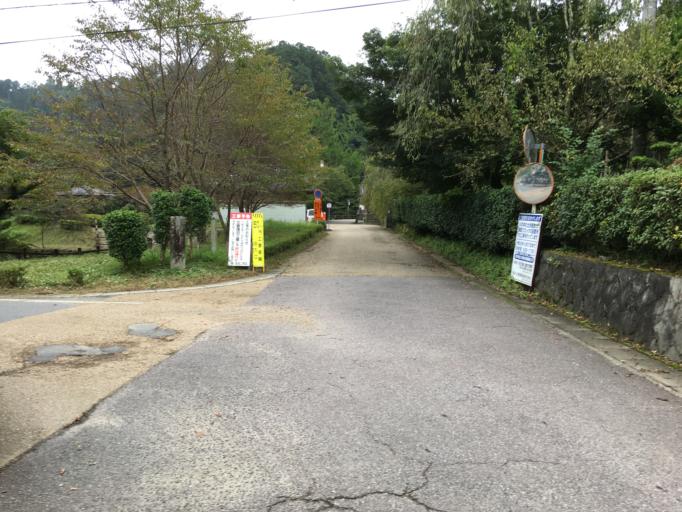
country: JP
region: Nara
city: Haibara-akanedai
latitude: 34.5634
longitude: 136.0157
